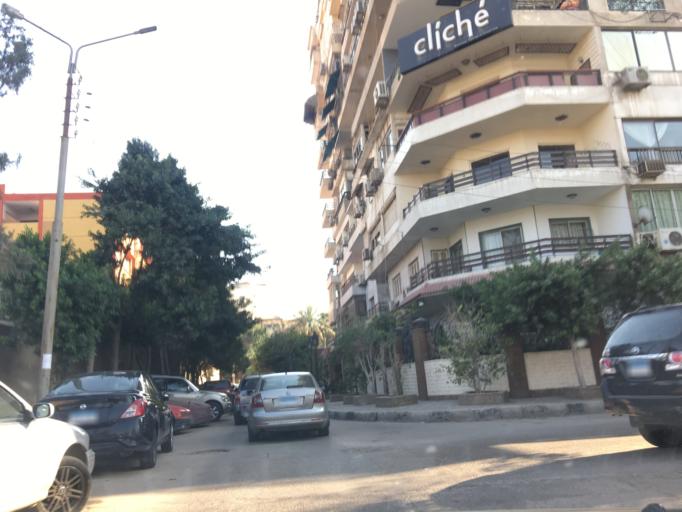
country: EG
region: Muhafazat al Qahirah
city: Cairo
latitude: 30.0891
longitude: 31.3328
